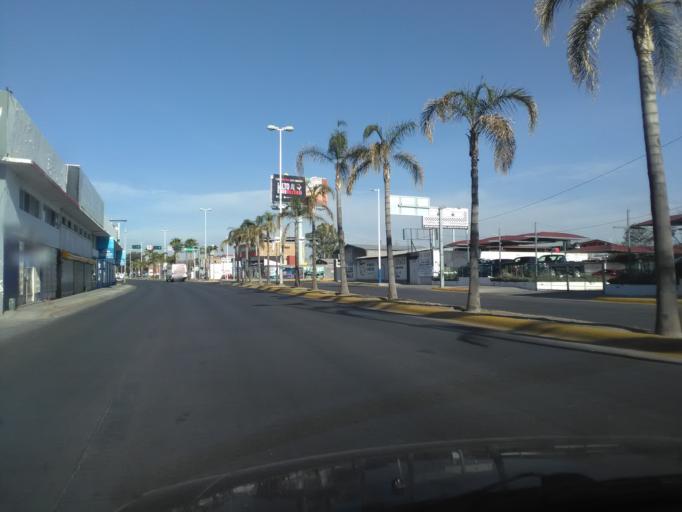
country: MX
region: Durango
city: Victoria de Durango
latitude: 24.0355
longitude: -104.6592
